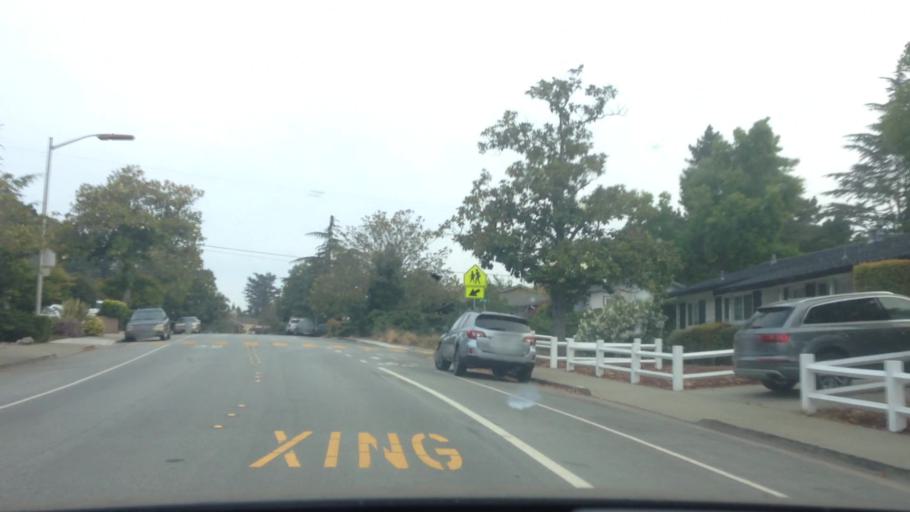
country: US
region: California
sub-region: San Mateo County
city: Emerald Lake Hills
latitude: 37.4580
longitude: -122.2561
